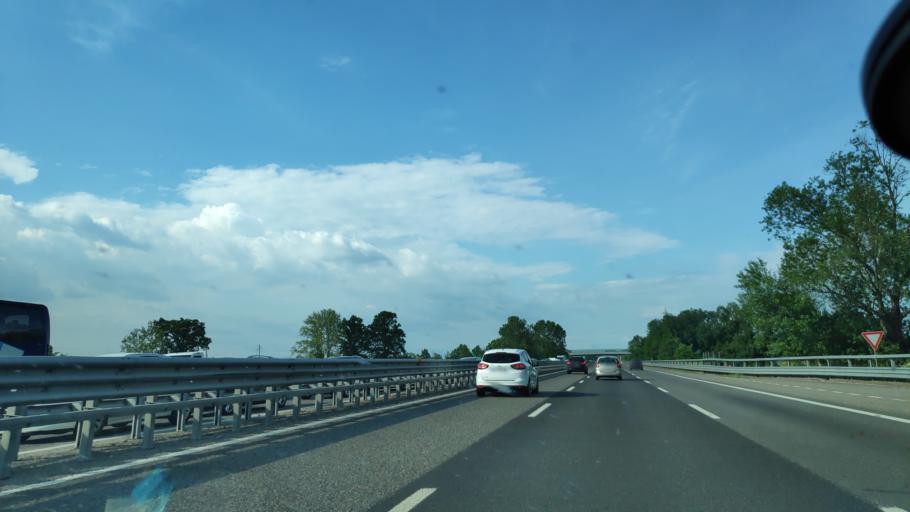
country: IT
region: Lombardy
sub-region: Citta metropolitana di Milano
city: Zibido San Giacomo
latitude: 45.3699
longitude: 9.1257
